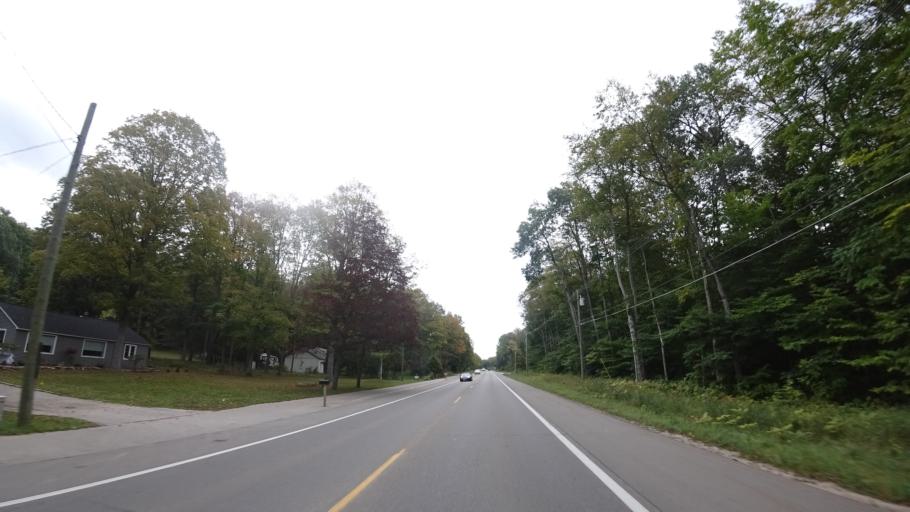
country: US
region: Michigan
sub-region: Emmet County
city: Petoskey
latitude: 45.4297
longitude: -84.9261
